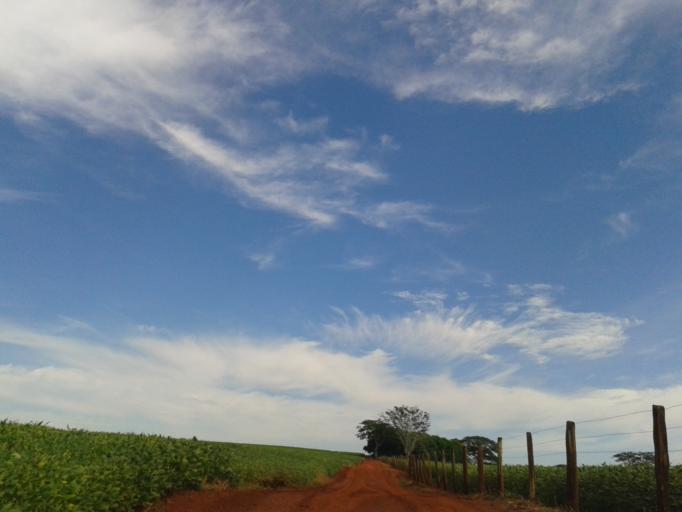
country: BR
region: Minas Gerais
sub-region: Capinopolis
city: Capinopolis
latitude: -18.6455
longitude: -49.7140
